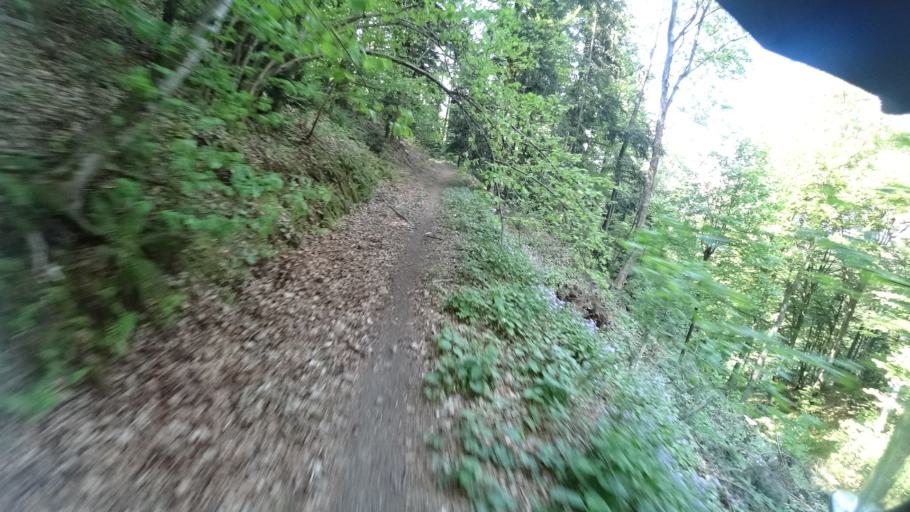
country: HR
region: Grad Zagreb
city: Kasina
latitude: 45.9417
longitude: 15.9928
